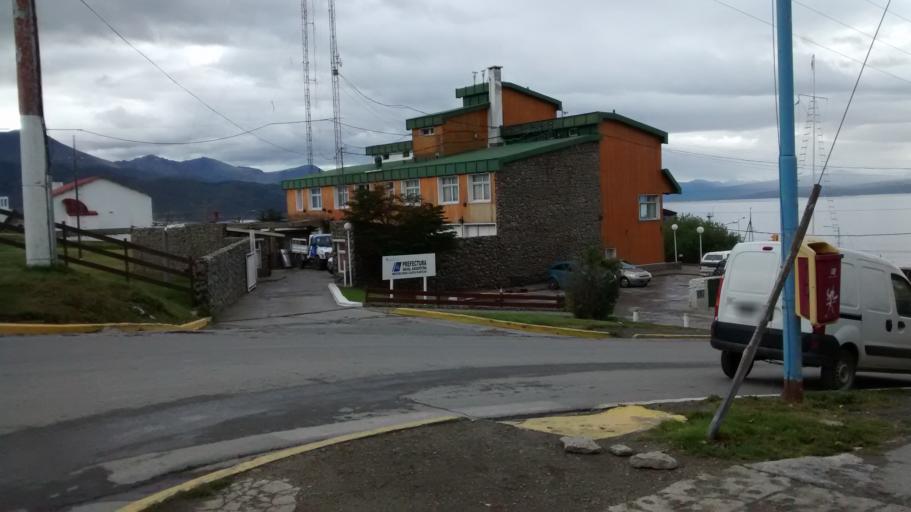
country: AR
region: Tierra del Fuego
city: Ushuaia
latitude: -54.8049
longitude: -68.2984
